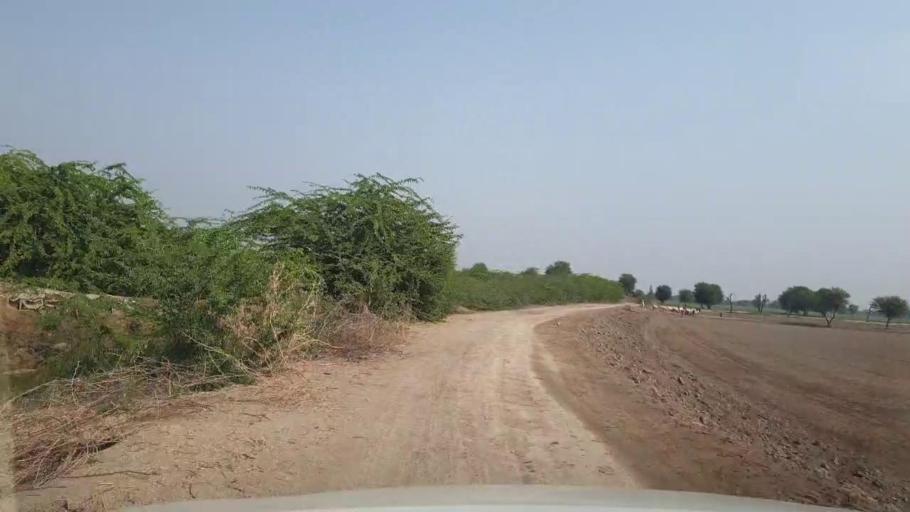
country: PK
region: Sindh
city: Chor
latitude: 25.4700
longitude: 69.7087
